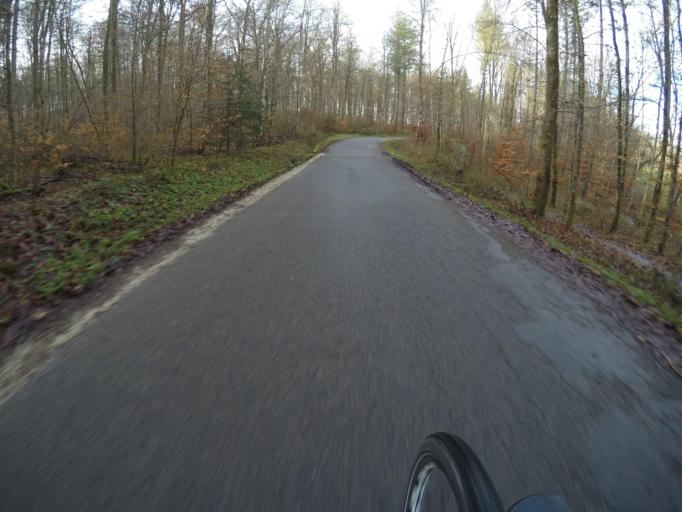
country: DE
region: Baden-Wuerttemberg
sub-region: Regierungsbezirk Stuttgart
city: Dettingen unter Teck
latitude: 48.6320
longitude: 9.4116
